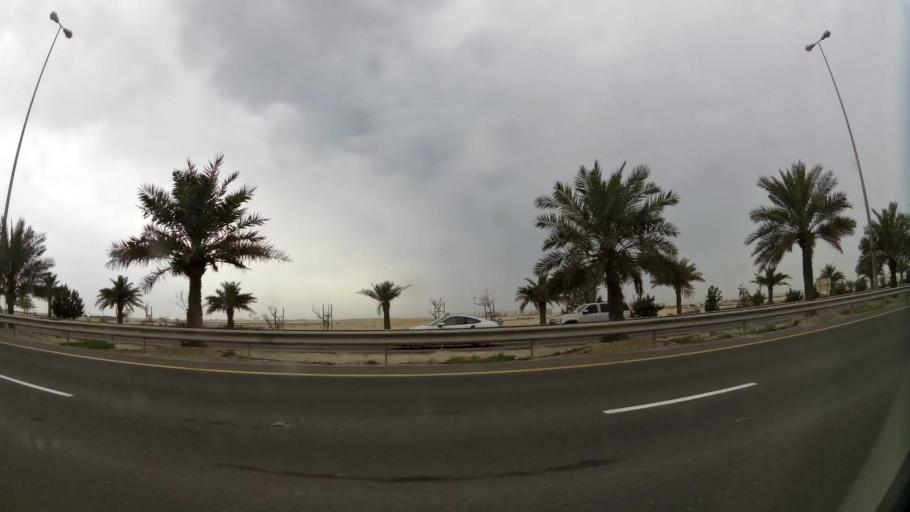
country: BH
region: Central Governorate
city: Dar Kulayb
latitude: 26.0823
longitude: 50.5397
